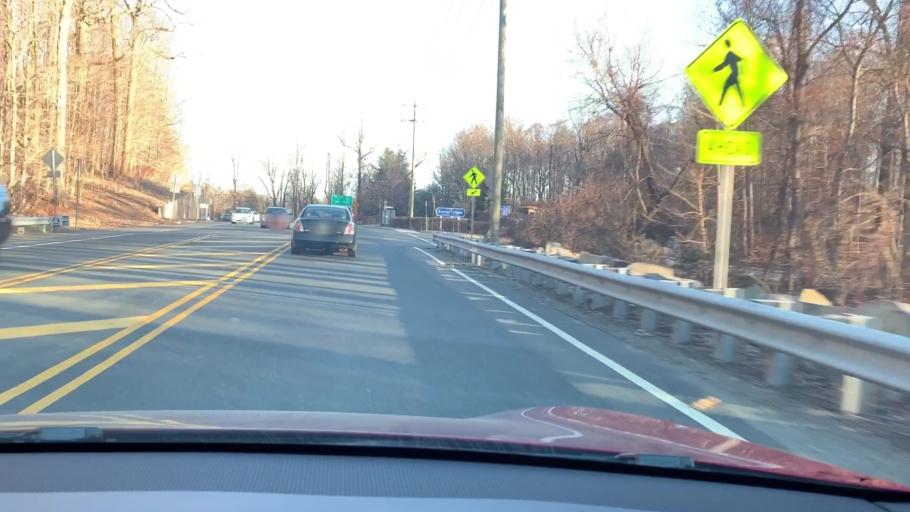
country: US
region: New York
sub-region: Westchester County
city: Hastings-on-Hudson
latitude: 41.0002
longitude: -73.9116
